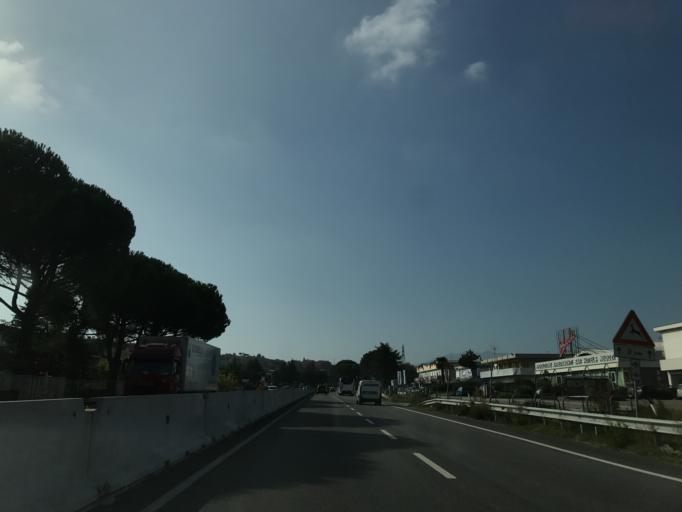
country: IT
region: Emilia-Romagna
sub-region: Provincia di Rimini
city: Cerasolo
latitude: 43.9940
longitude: 12.5377
